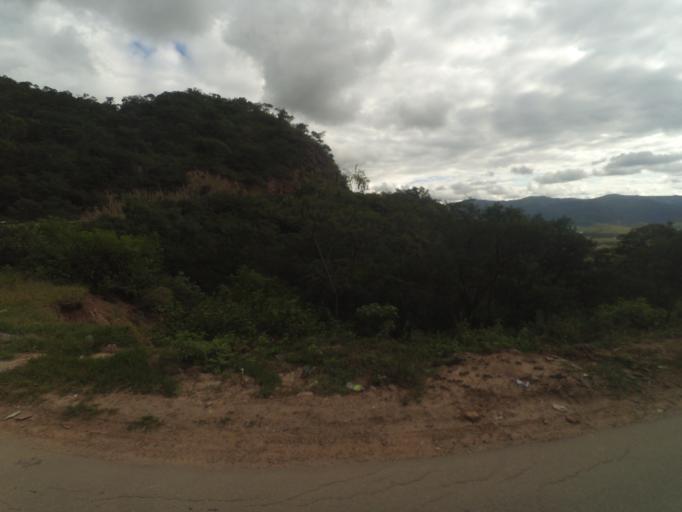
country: BO
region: Santa Cruz
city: Samaipata
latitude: -18.1656
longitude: -63.9024
